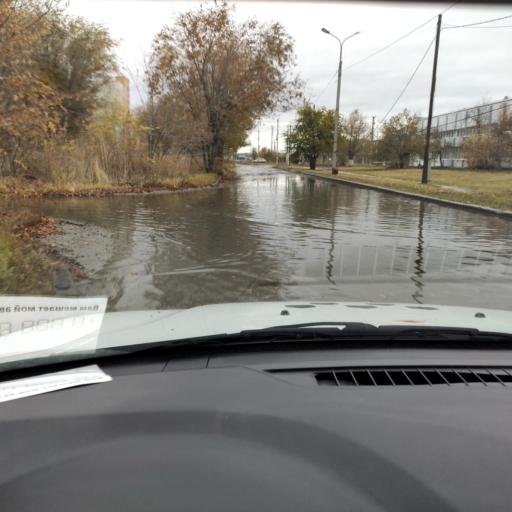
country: RU
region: Samara
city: Tol'yatti
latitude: 53.5589
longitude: 49.3007
